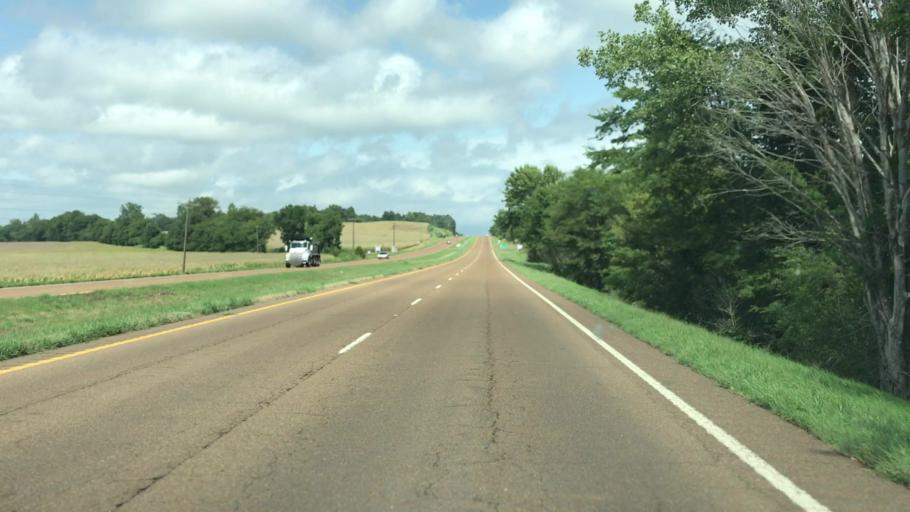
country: US
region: Tennessee
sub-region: Obion County
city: Englewood
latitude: 36.3665
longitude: -89.1271
